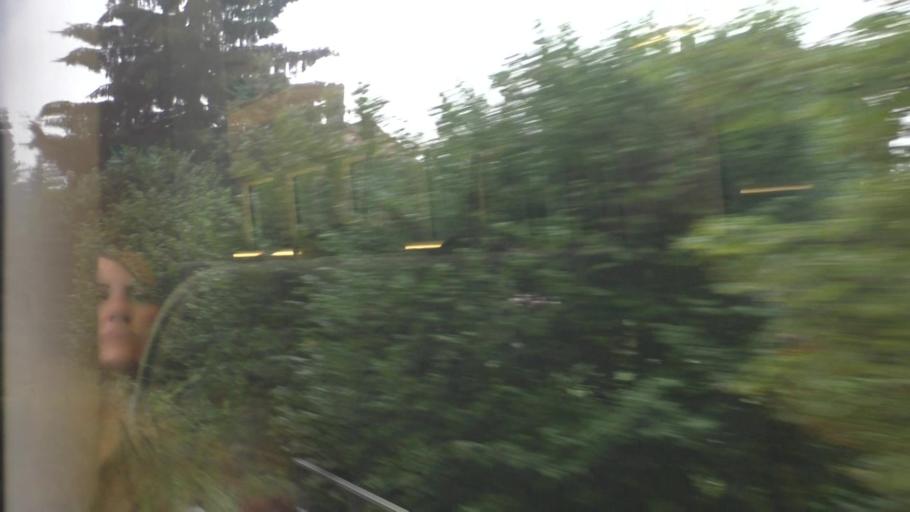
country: DE
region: Saxony
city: Ebersbach
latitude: 50.9906
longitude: 14.5884
